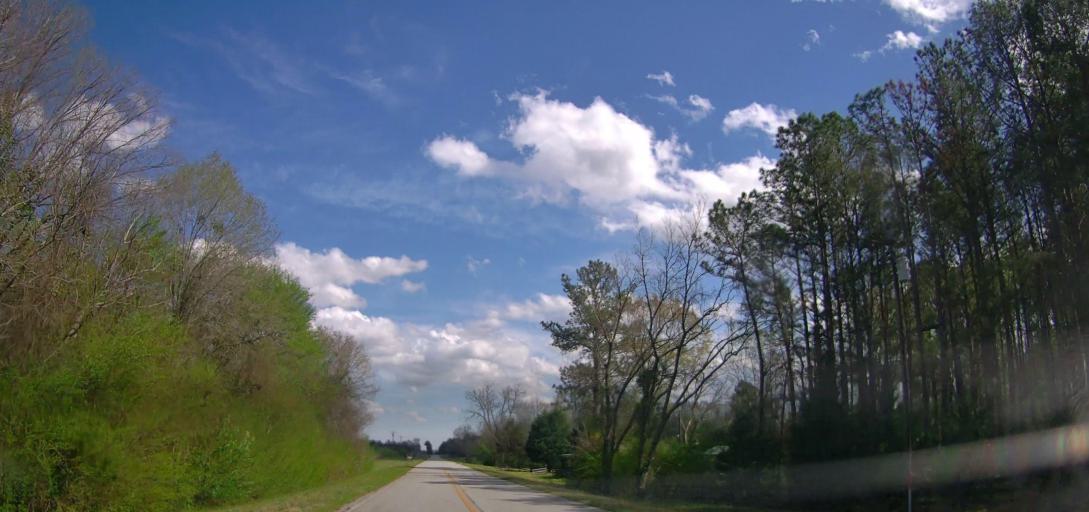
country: US
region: Georgia
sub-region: Wilkinson County
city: Gordon
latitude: 32.8349
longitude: -83.4338
